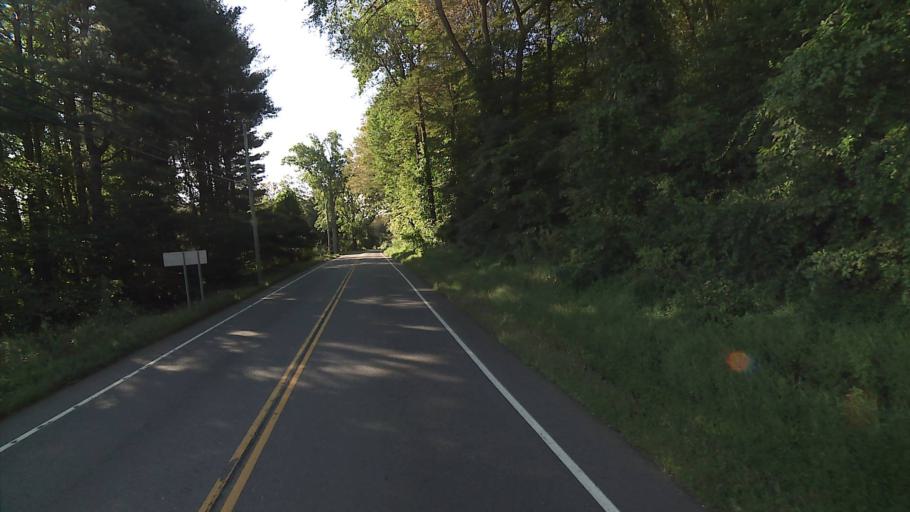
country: US
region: Connecticut
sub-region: New London County
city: Baltic
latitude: 41.6057
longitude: -72.1371
